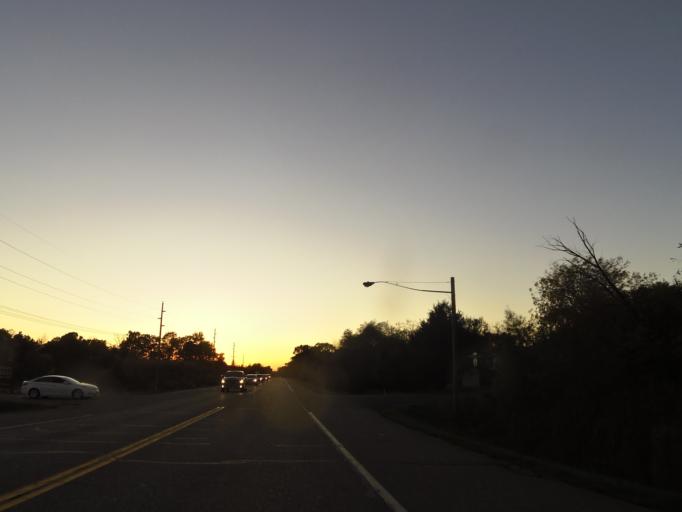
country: US
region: Minnesota
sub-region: Dakota County
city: Eagan
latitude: 44.7902
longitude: -93.1237
